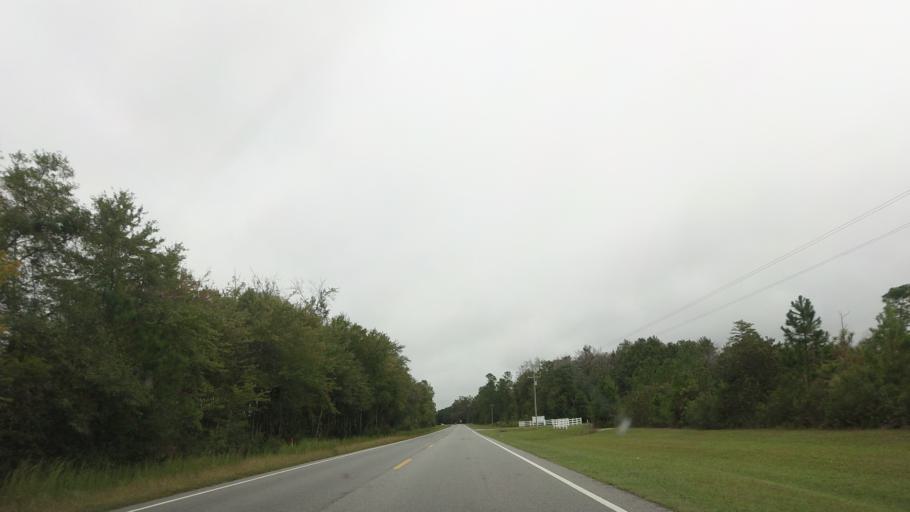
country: US
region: Georgia
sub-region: Berrien County
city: Nashville
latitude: 31.2982
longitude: -83.2346
